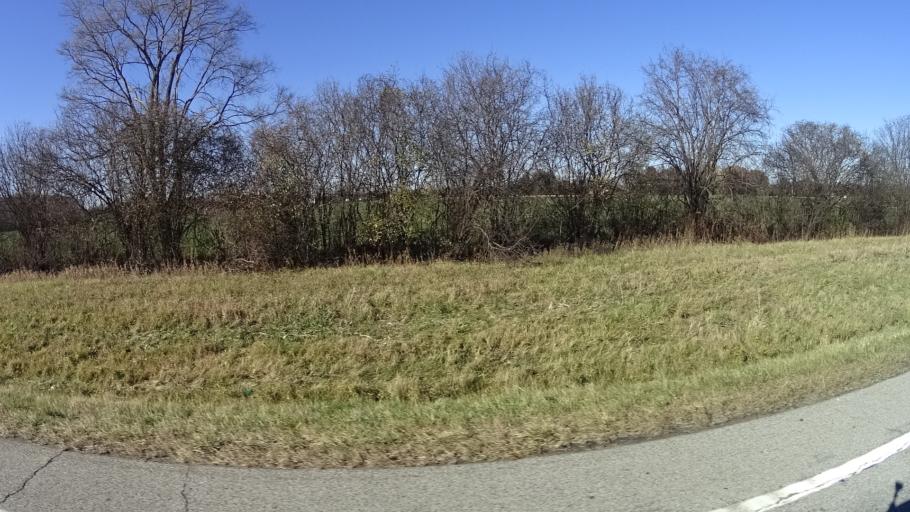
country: US
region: Ohio
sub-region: Lorain County
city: Oberlin
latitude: 41.2773
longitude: -82.1900
